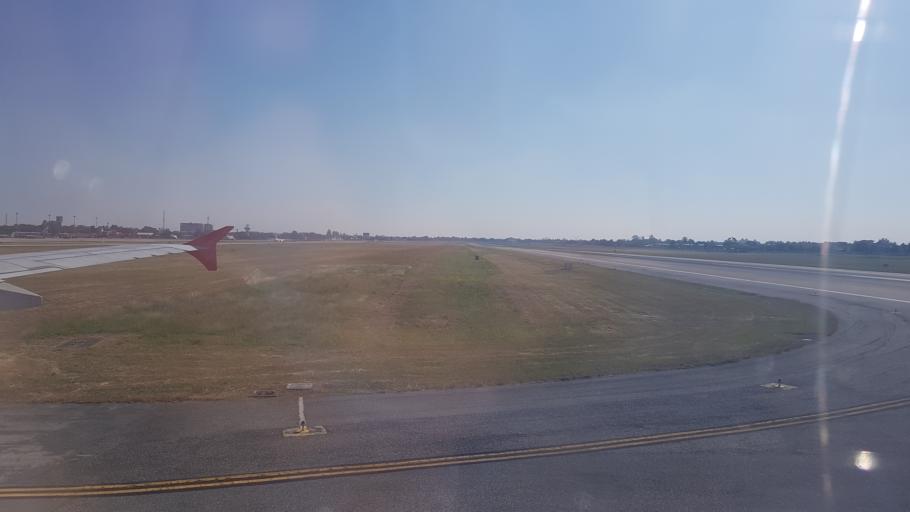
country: TH
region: Chiang Mai
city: Chiang Mai
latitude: 18.7720
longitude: 98.9627
